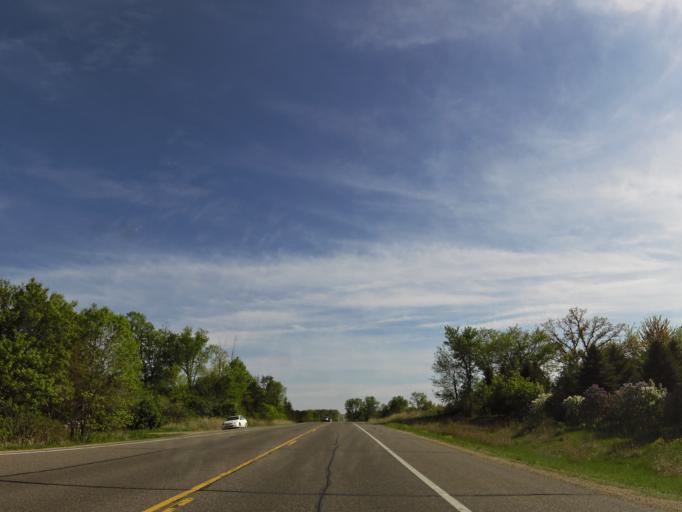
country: US
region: Minnesota
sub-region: Washington County
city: Oakdale
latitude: 44.9858
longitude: -92.9340
